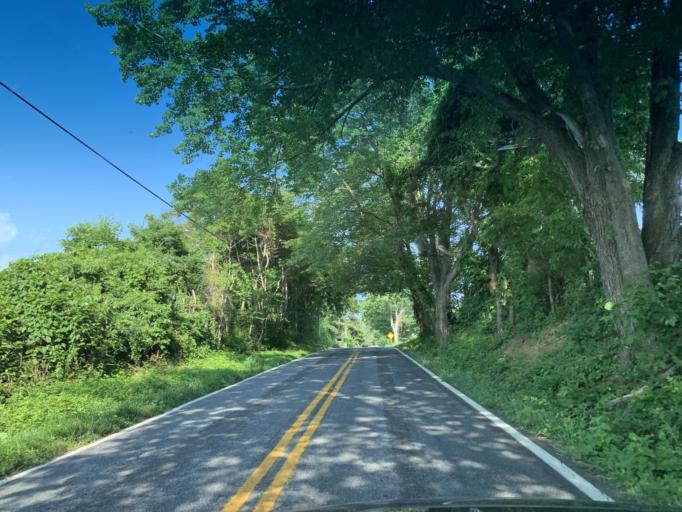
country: US
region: Maryland
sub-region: Frederick County
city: Urbana
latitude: 39.2480
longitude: -77.3584
